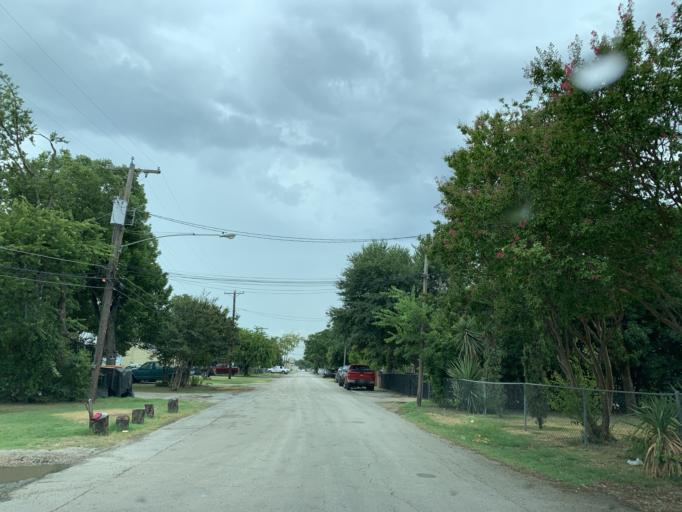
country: US
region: Texas
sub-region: Dallas County
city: Duncanville
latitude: 32.6688
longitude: -96.8302
